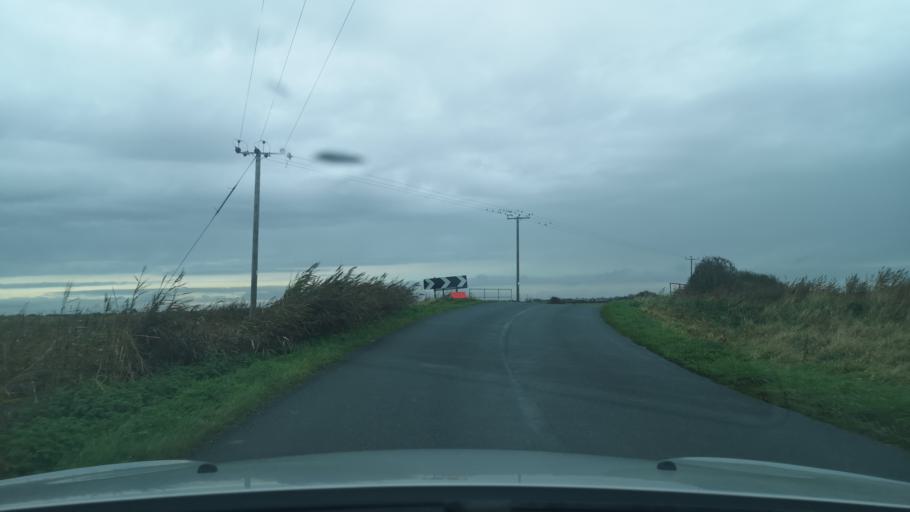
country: GB
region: England
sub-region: East Riding of Yorkshire
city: Easington
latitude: 53.6288
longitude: 0.1235
